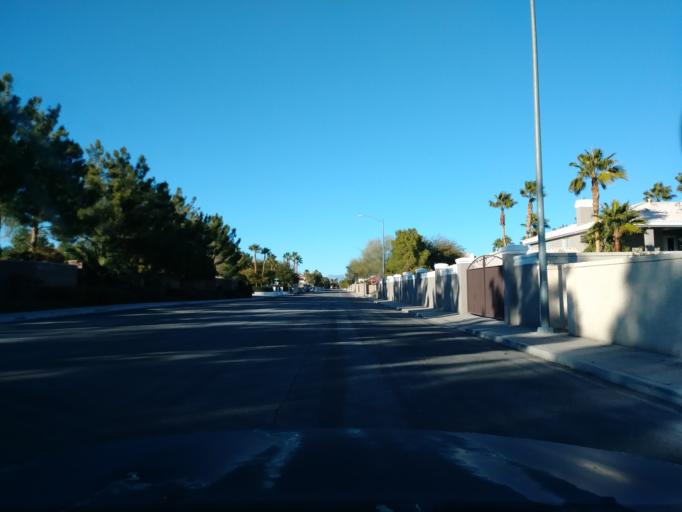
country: US
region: Nevada
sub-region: Clark County
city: Spring Valley
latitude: 36.1468
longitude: -115.2679
